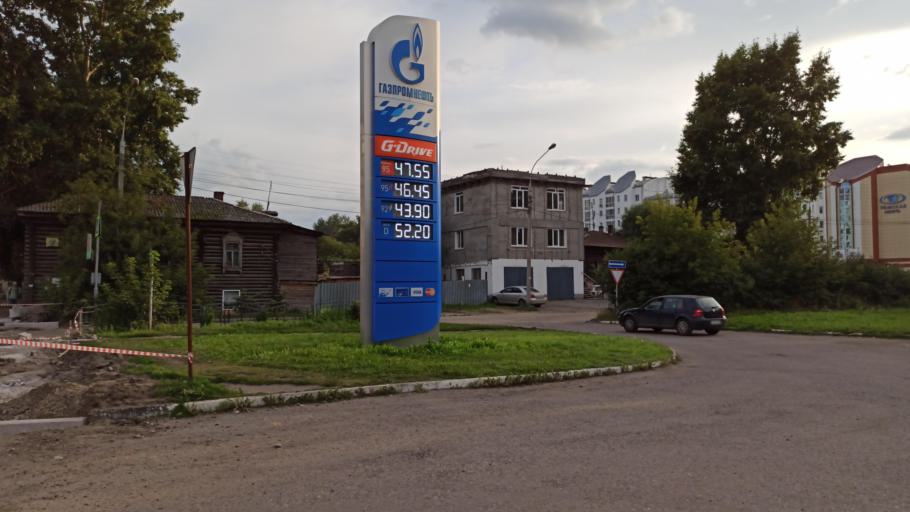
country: RU
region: Tomsk
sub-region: Tomskiy Rayon
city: Tomsk
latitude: 56.4829
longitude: 84.9661
